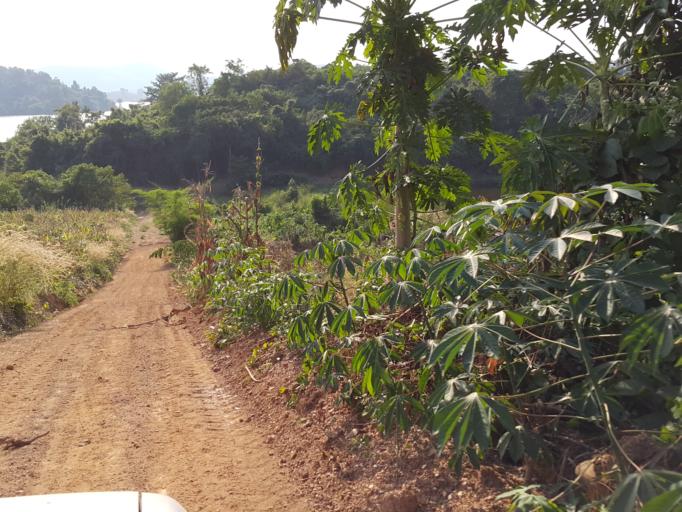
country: TH
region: Sukhothai
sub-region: Amphoe Si Satchanalai
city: Si Satchanalai
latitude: 17.4912
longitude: 99.6255
